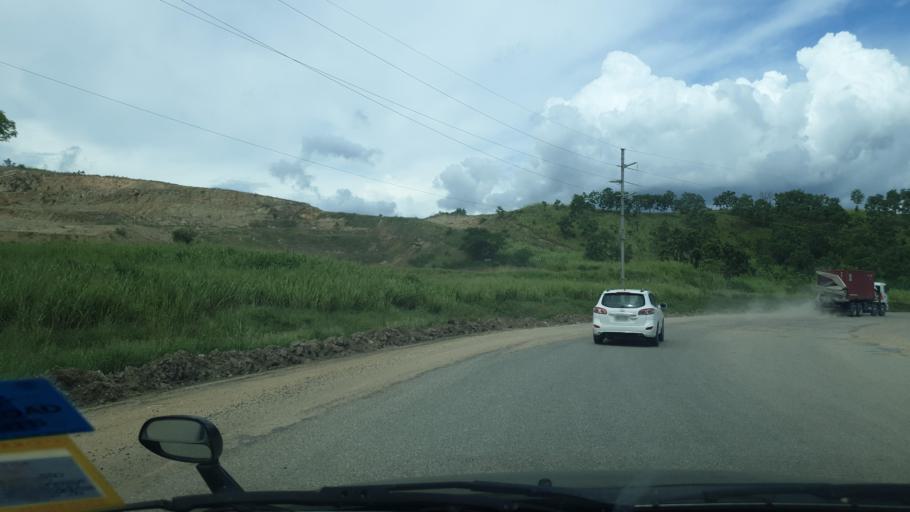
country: PG
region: National Capital
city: Port Moresby
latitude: -9.4151
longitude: 147.1008
